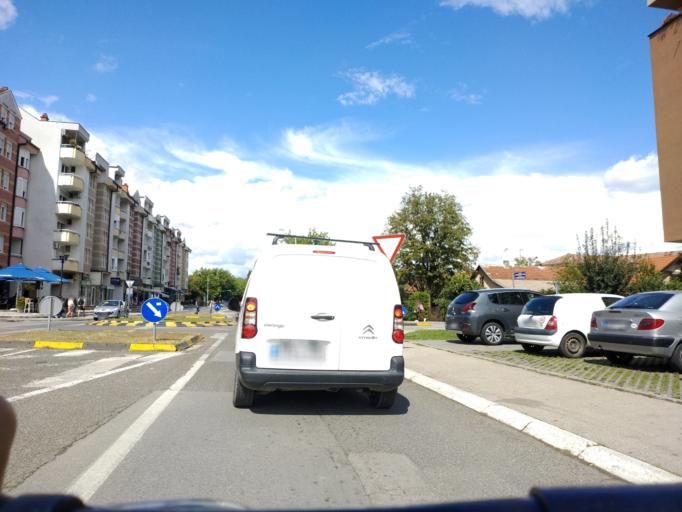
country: BA
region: Republika Srpska
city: Mejdan - Obilicevo
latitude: 44.7629
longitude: 17.2010
